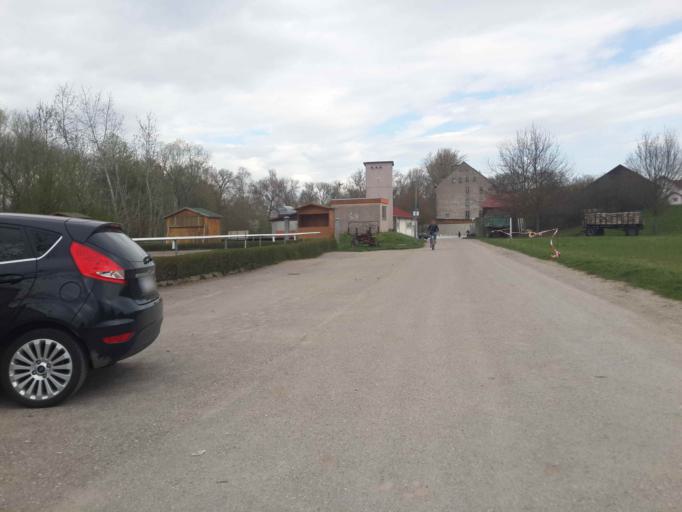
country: DE
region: Baden-Wuerttemberg
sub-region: Regierungsbezirk Stuttgart
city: Untereisesheim
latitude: 49.2245
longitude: 9.2127
